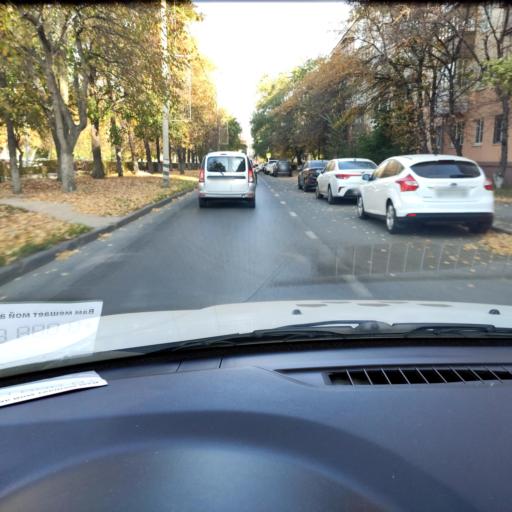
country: RU
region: Samara
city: Tol'yatti
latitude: 53.5088
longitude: 49.4118
